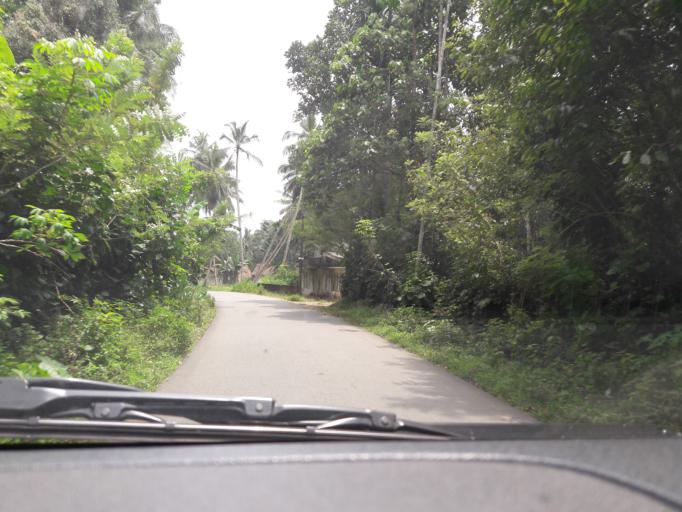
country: LK
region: Southern
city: Galle
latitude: 6.1818
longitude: 80.3014
